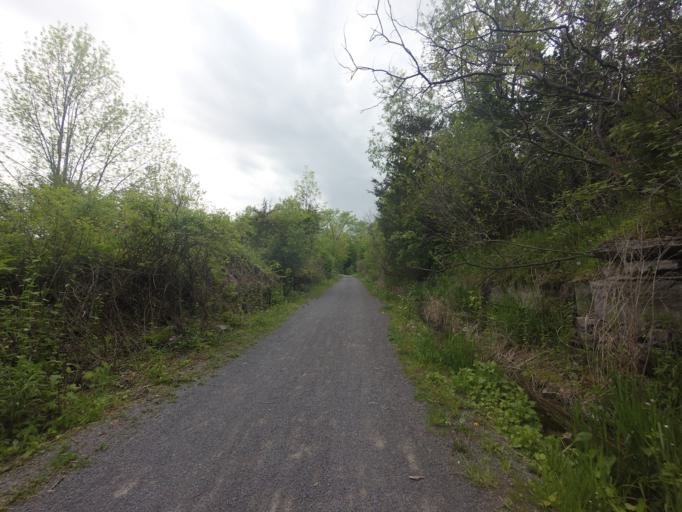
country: CA
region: Ontario
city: Kingston
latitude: 44.2999
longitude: -76.5709
